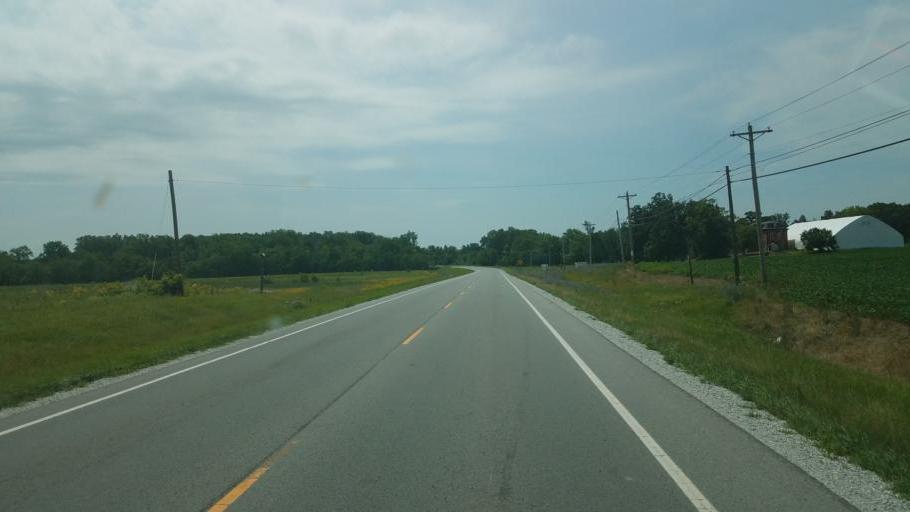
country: US
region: Ohio
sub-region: Wyandot County
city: Carey
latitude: 40.9272
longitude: -83.3504
